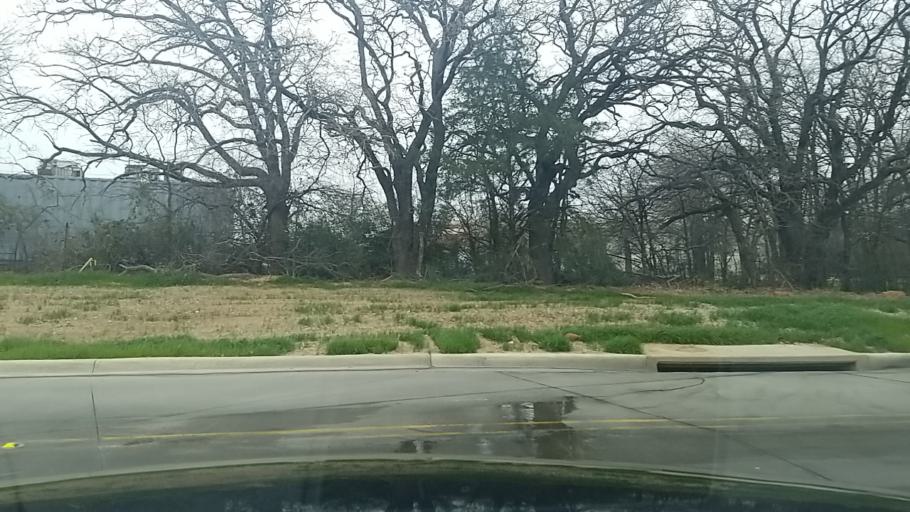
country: US
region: Texas
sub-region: Denton County
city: Corinth
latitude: 33.1784
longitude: -97.0998
